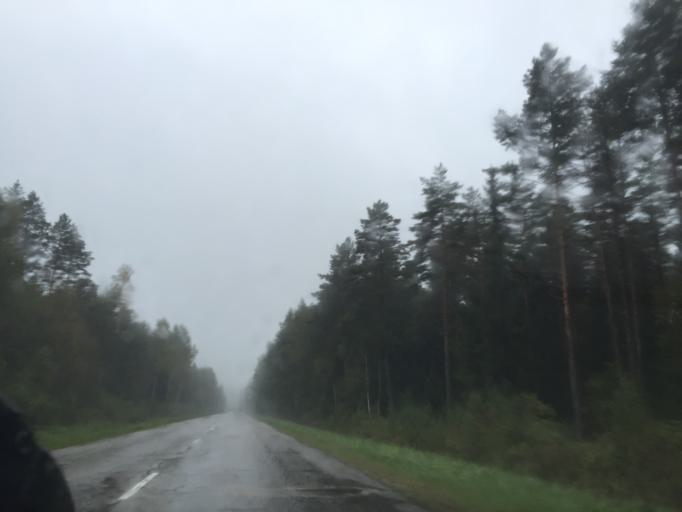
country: LV
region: Ropazu
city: Ropazi
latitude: 56.9934
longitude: 24.6431
